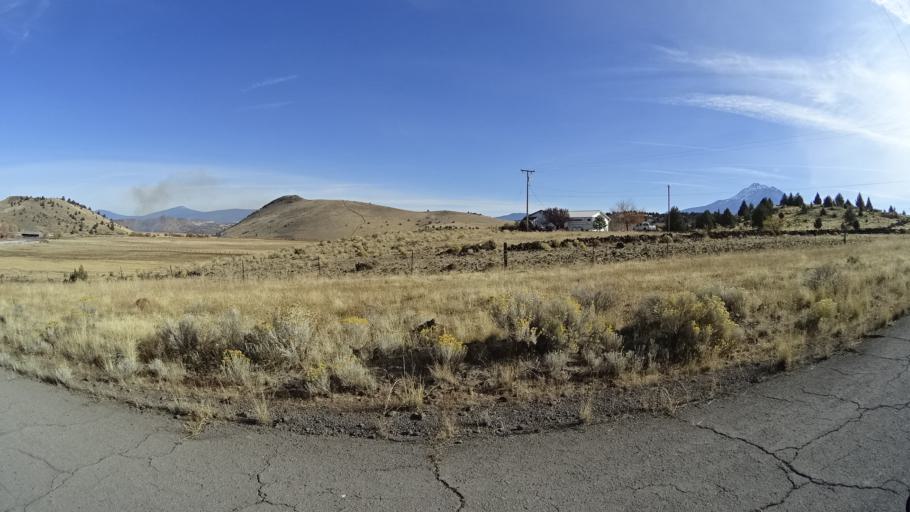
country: US
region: California
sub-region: Siskiyou County
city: Weed
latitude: 41.4988
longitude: -122.4555
